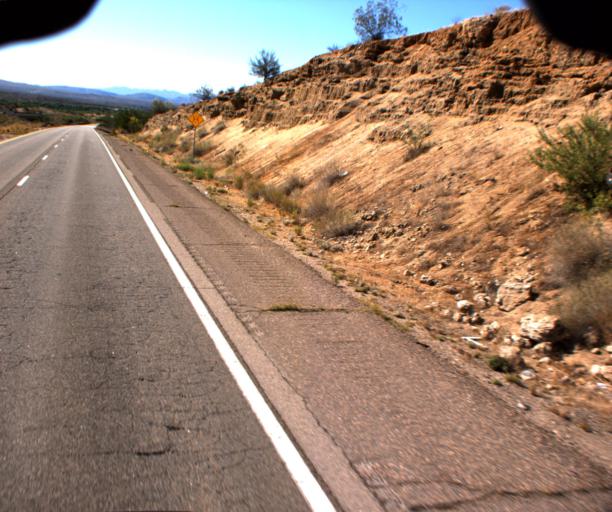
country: US
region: Arizona
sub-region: Yavapai County
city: Bagdad
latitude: 34.6784
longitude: -113.5935
